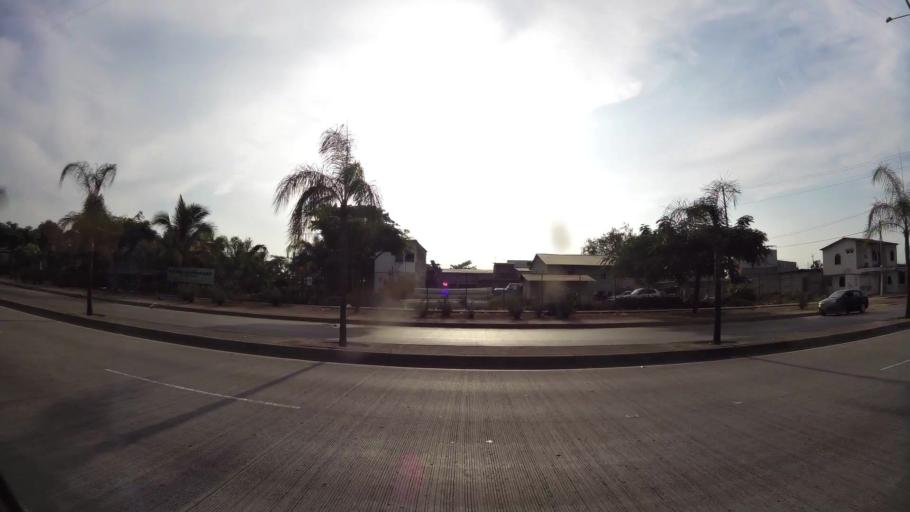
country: EC
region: Guayas
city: Eloy Alfaro
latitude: -2.0878
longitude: -79.8960
